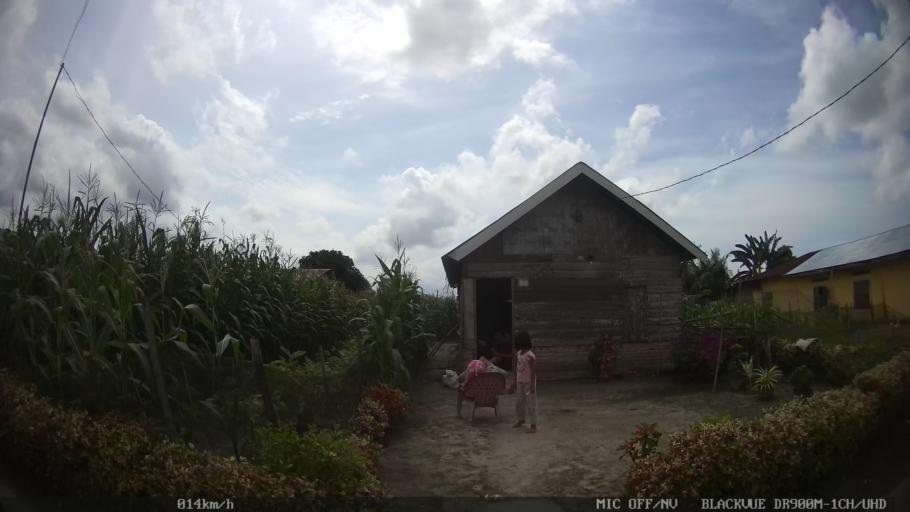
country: ID
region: North Sumatra
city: Percut
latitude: 3.5710
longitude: 98.8502
